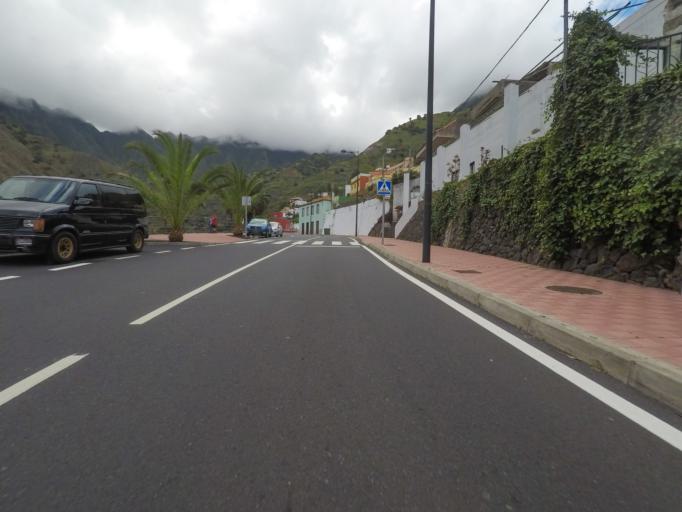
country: ES
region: Canary Islands
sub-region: Provincia de Santa Cruz de Tenerife
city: Hermigua
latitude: 28.1510
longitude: -17.1982
